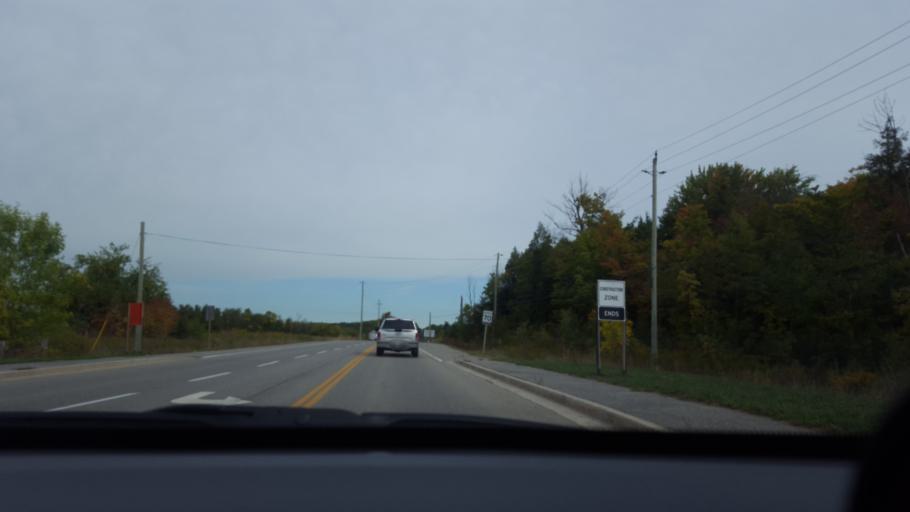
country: CA
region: Ontario
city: Vaughan
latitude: 43.9476
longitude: -79.5333
